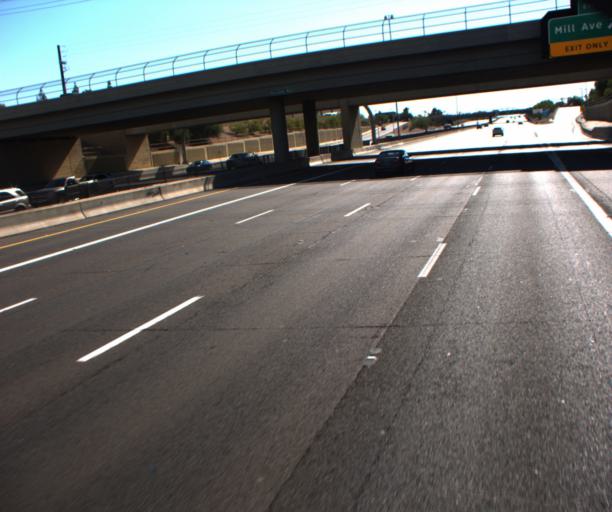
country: US
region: Arizona
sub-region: Maricopa County
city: Guadalupe
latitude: 33.3854
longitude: -111.9442
